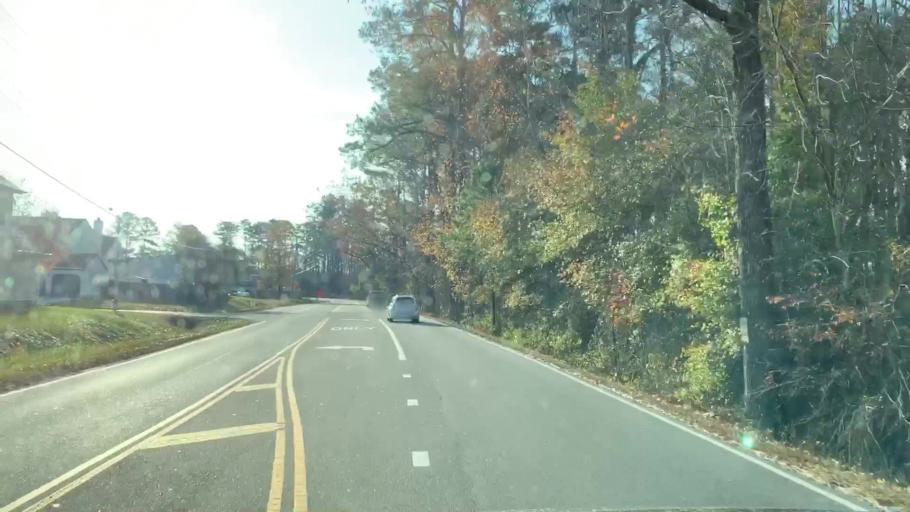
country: US
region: Virginia
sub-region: City of Chesapeake
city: Chesapeake
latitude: 36.7637
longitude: -76.1488
